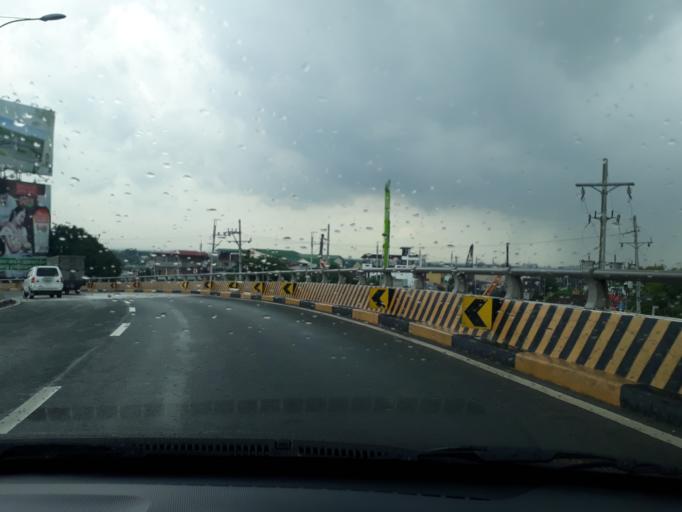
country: PH
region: Metro Manila
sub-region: Makati City
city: Makati City
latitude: 14.5116
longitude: 121.0326
